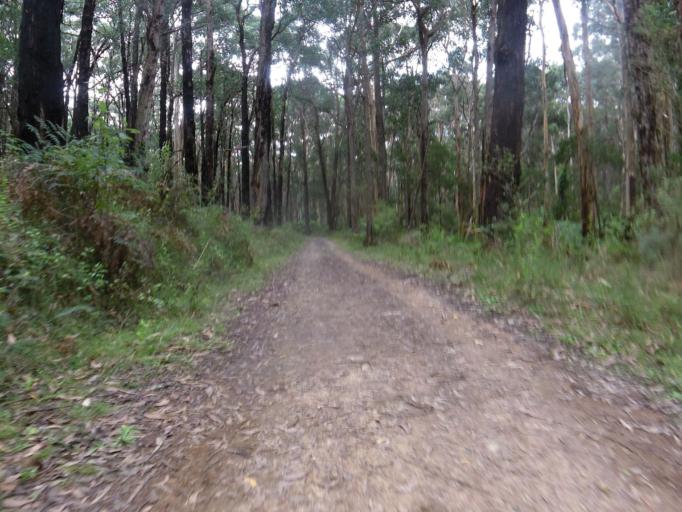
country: AU
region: Victoria
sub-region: Knox
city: The Basin
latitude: -37.8475
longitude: 145.3392
